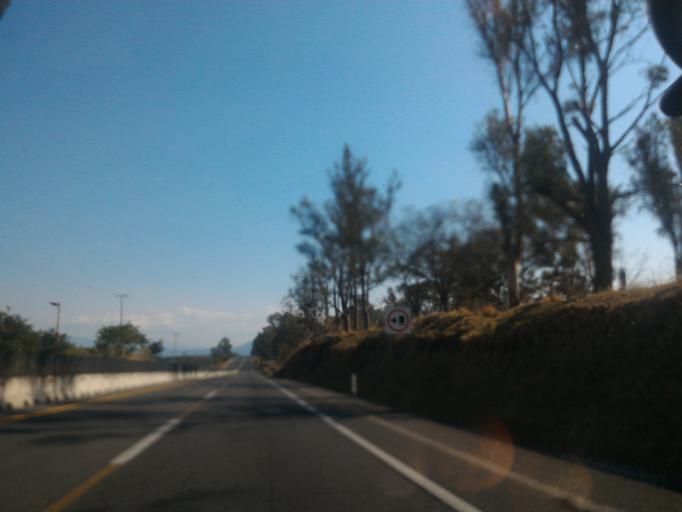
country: MX
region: Jalisco
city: Zapotiltic
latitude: 19.6102
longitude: -103.4585
